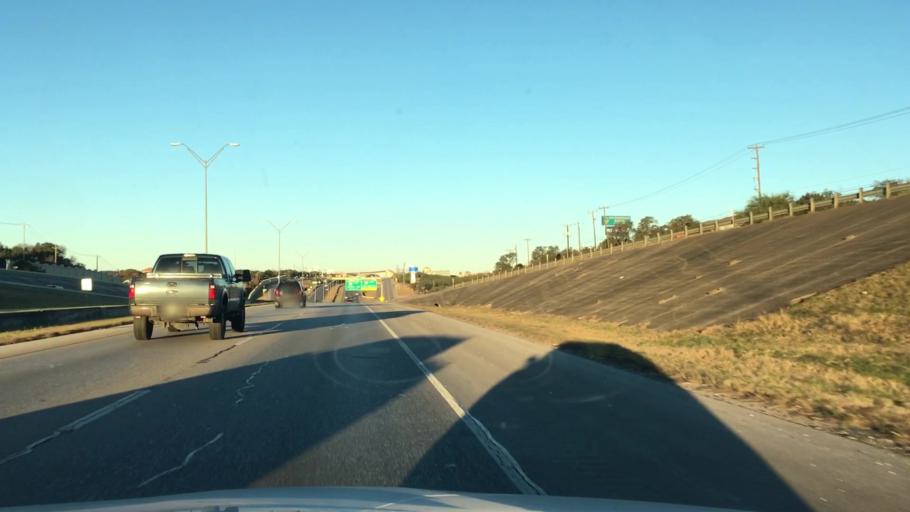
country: US
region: Texas
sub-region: Bexar County
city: Hollywood Park
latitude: 29.5921
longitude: -98.4461
